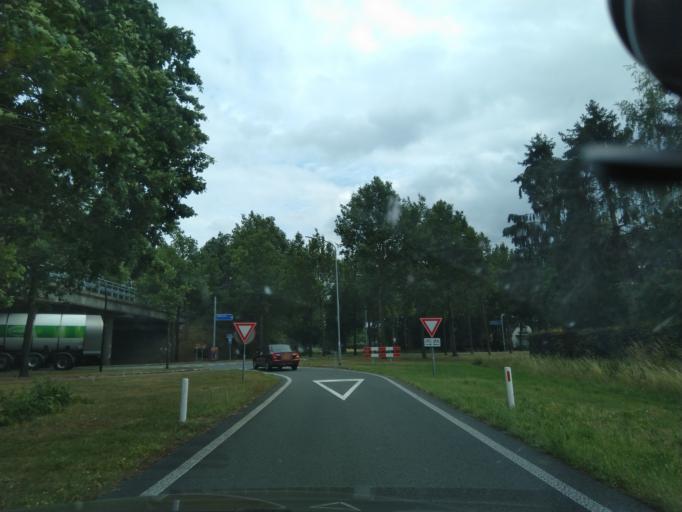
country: NL
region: Groningen
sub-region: Gemeente  Oldambt
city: Winschoten
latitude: 53.1003
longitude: 7.0735
